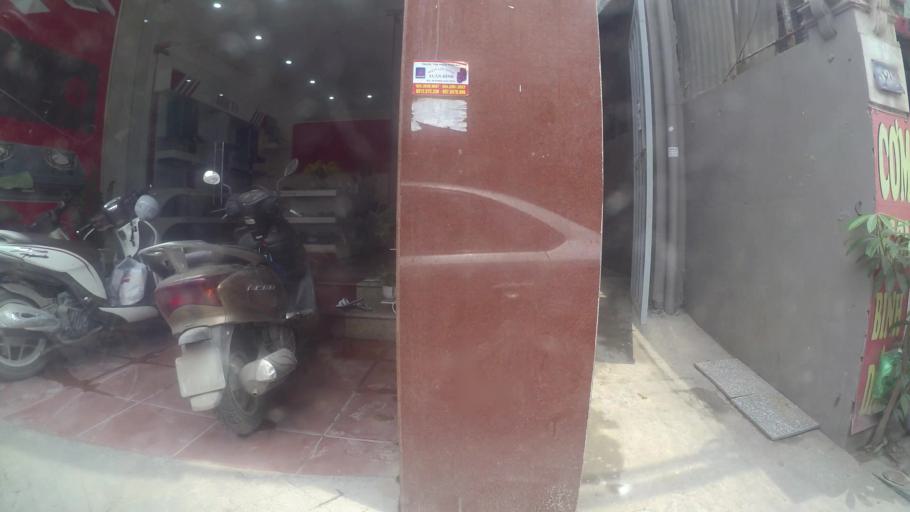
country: VN
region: Ha Noi
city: Tay Ho
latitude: 21.0757
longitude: 105.7881
